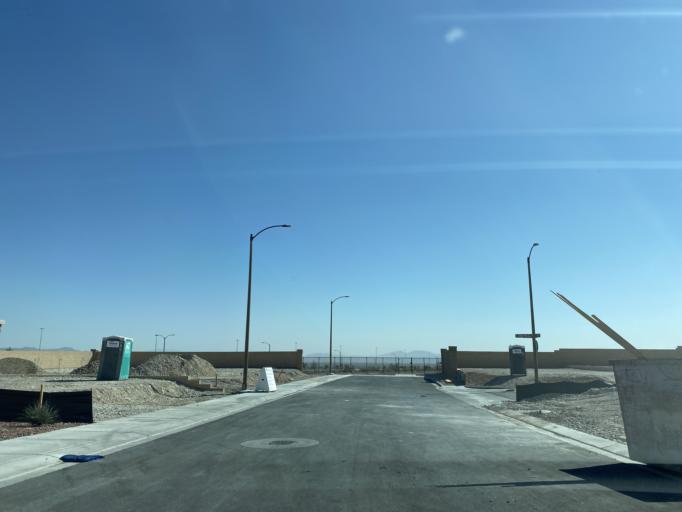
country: US
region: Nevada
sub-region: Clark County
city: Summerlin South
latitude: 36.3198
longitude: -115.3103
